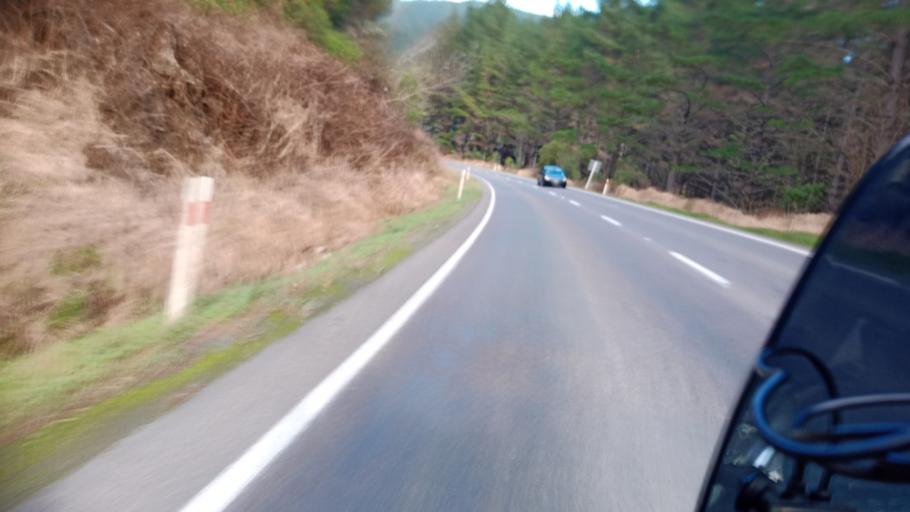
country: NZ
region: Gisborne
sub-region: Gisborne District
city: Gisborne
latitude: -38.8302
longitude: 177.8981
